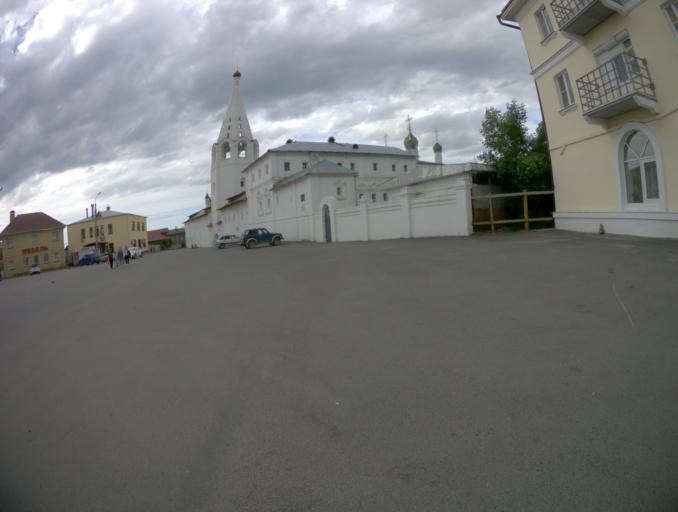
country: RU
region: Vladimir
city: Gorokhovets
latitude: 56.2063
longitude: 42.6790
